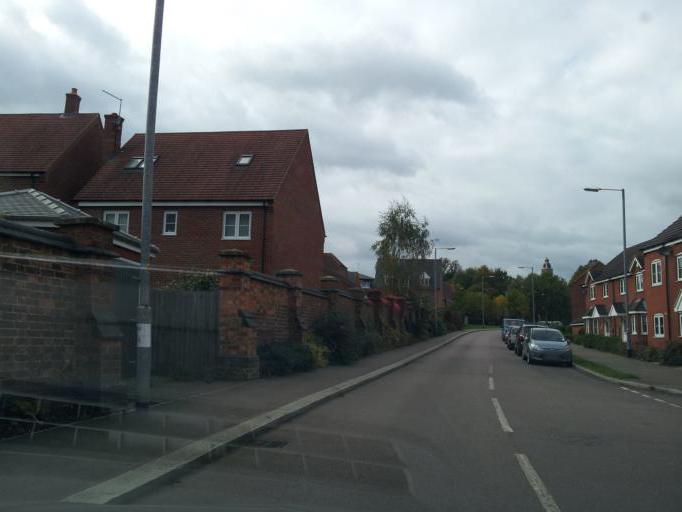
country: GB
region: England
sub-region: Northamptonshire
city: Blisworth
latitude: 52.2419
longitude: -0.9529
